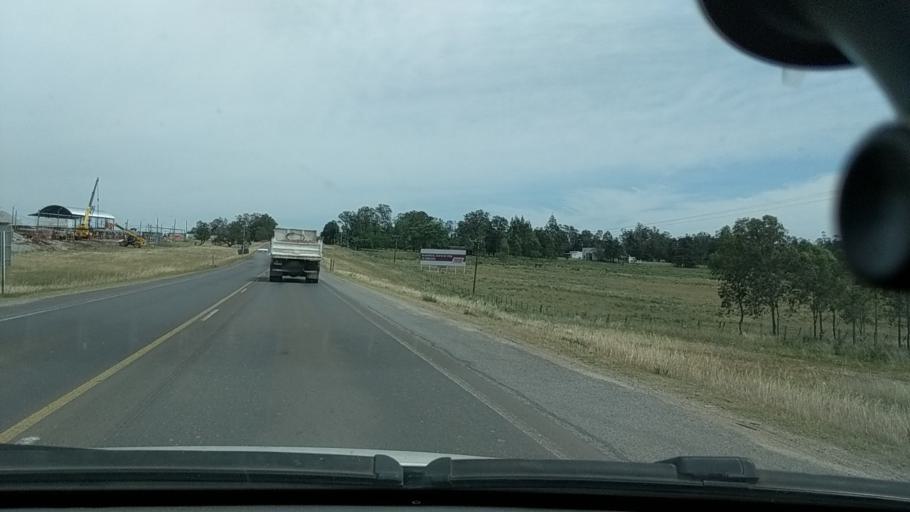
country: UY
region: Durazno
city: Durazno
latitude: -33.4217
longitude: -56.5026
